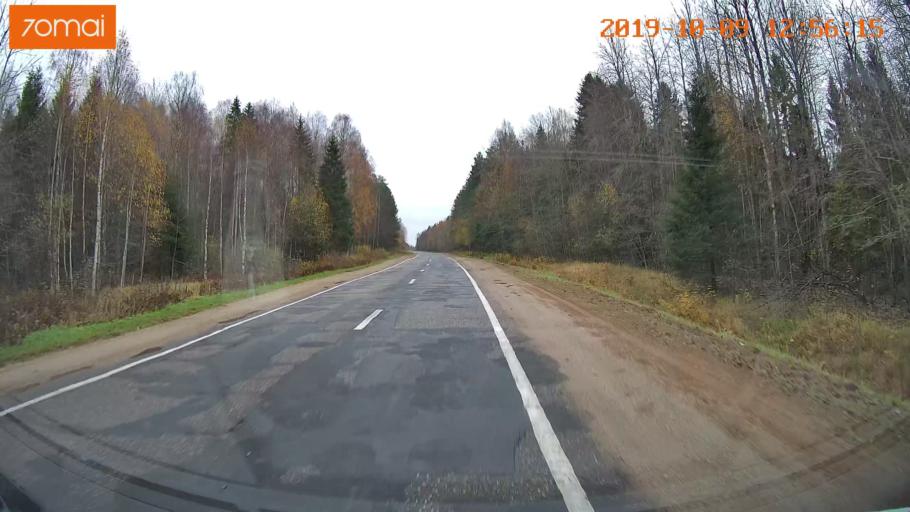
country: RU
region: Jaroslavl
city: Prechistoye
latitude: 58.3953
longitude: 40.4127
